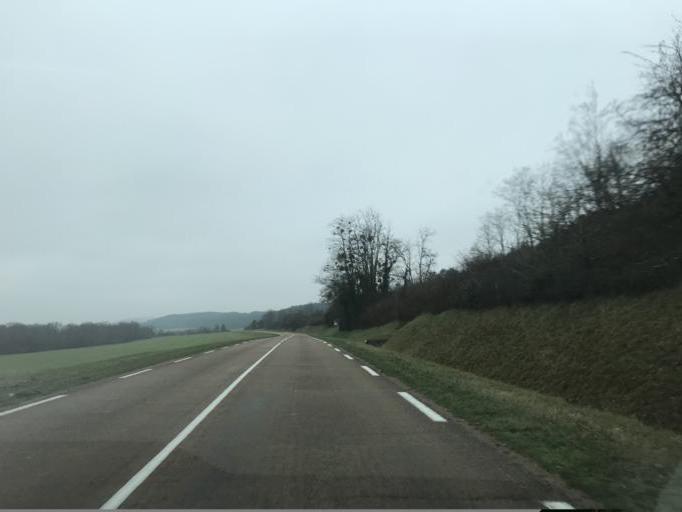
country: FR
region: Bourgogne
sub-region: Departement de l'Yonne
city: Avallon
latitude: 47.5143
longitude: 3.7677
